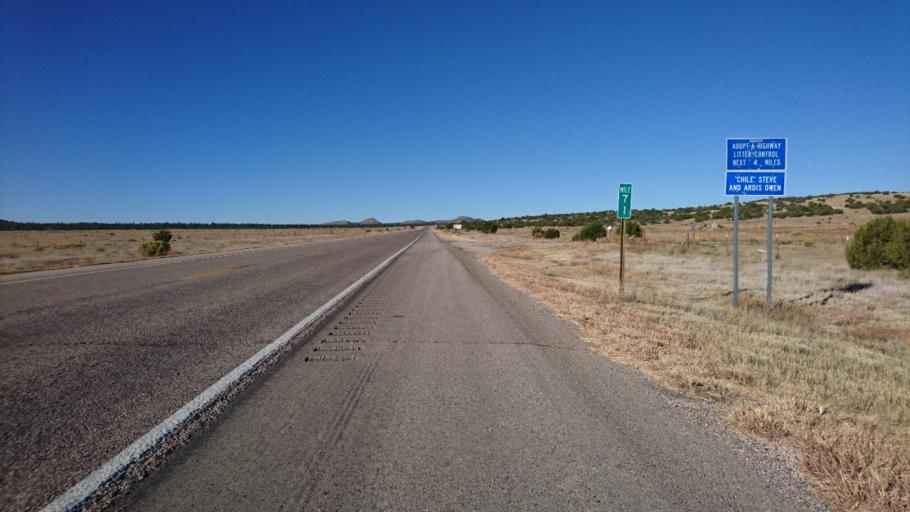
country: US
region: New Mexico
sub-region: Cibola County
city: Grants
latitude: 34.9595
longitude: -107.9239
